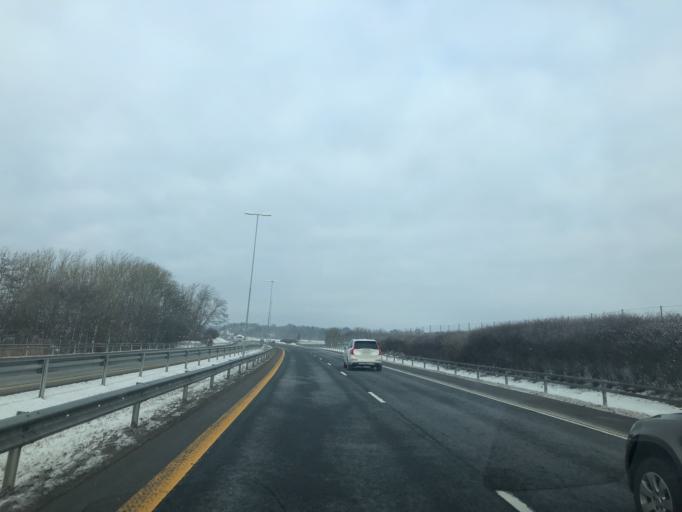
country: NO
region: Ostfold
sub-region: Sarpsborg
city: Skjeberg
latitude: 59.1455
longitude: 11.2511
